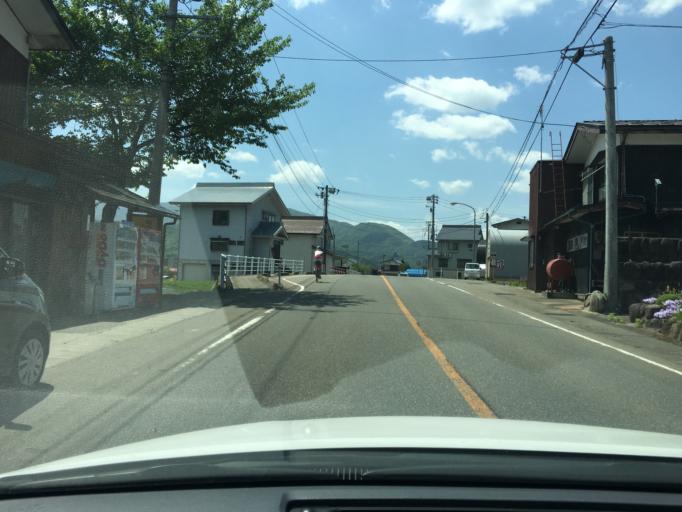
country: JP
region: Niigata
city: Tochio-honcho
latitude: 37.3295
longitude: 139.0265
